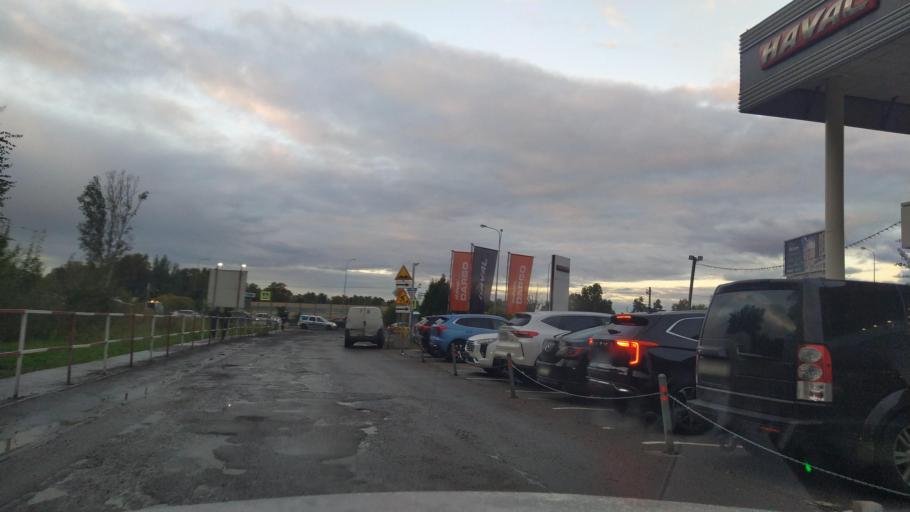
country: RU
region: St.-Petersburg
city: Lakhtinskiy
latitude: 59.9895
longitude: 30.1669
